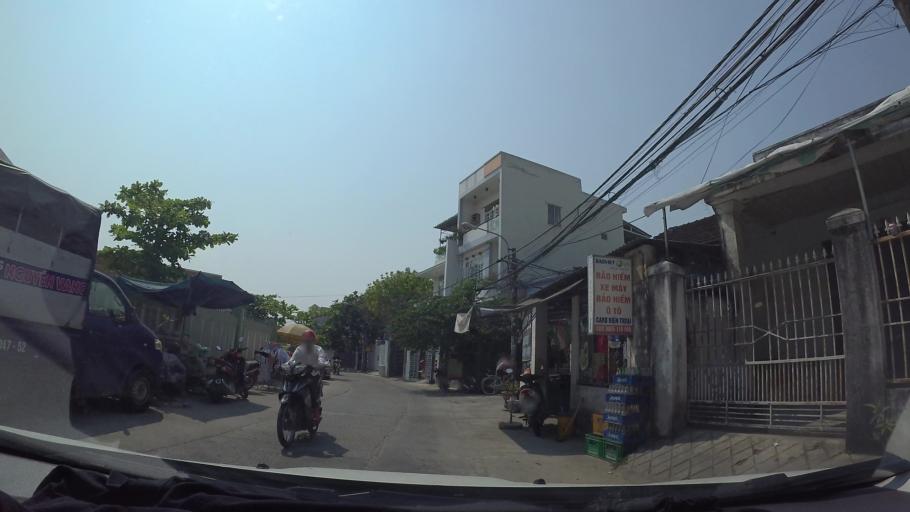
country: VN
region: Da Nang
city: Cam Le
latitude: 16.0110
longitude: 108.2046
